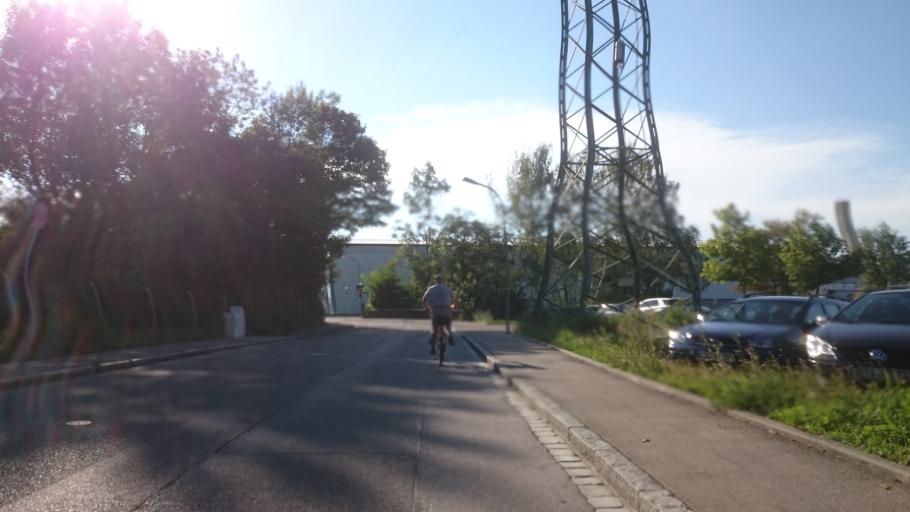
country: DE
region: Bavaria
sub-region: Swabia
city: Konigsbrunn
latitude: 48.3195
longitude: 10.9137
